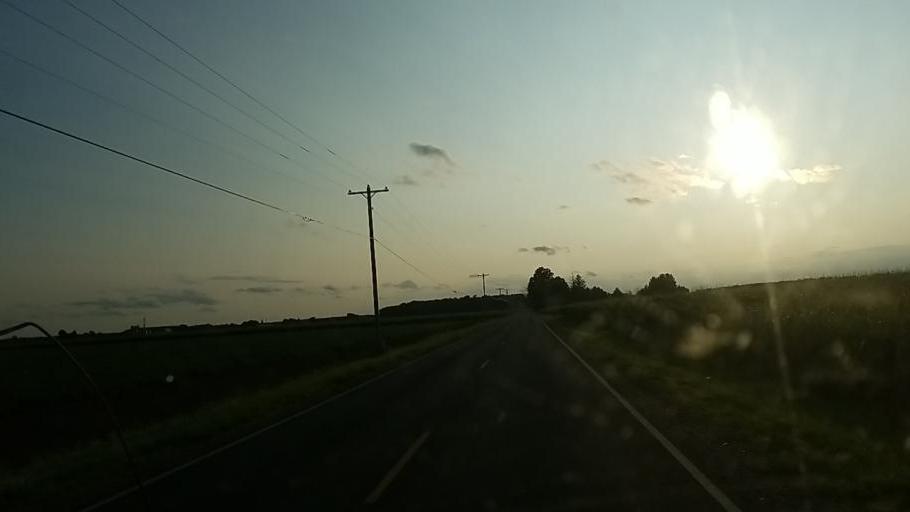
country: US
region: Michigan
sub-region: Montcalm County
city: Howard City
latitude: 43.3666
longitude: -85.4140
